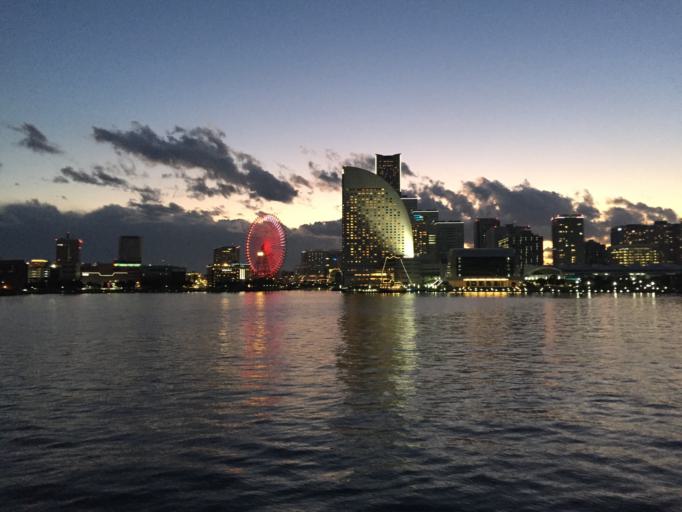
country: JP
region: Kanagawa
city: Yokohama
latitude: 35.4611
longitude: 139.6438
